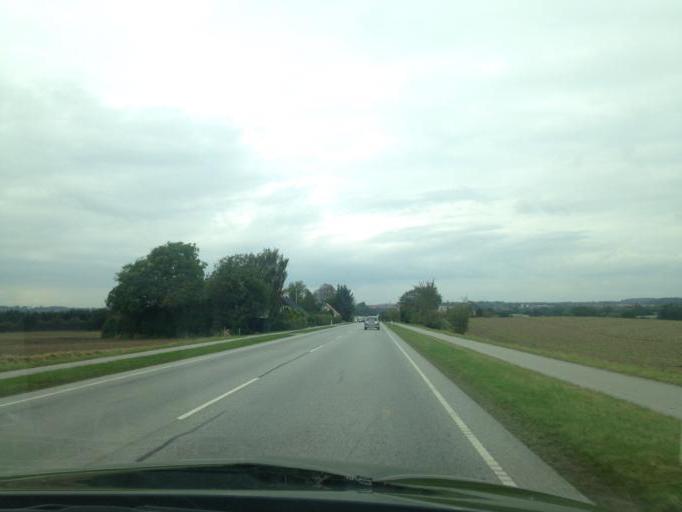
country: DK
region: South Denmark
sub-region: Kolding Kommune
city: Christiansfeld
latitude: 55.3337
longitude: 9.4907
